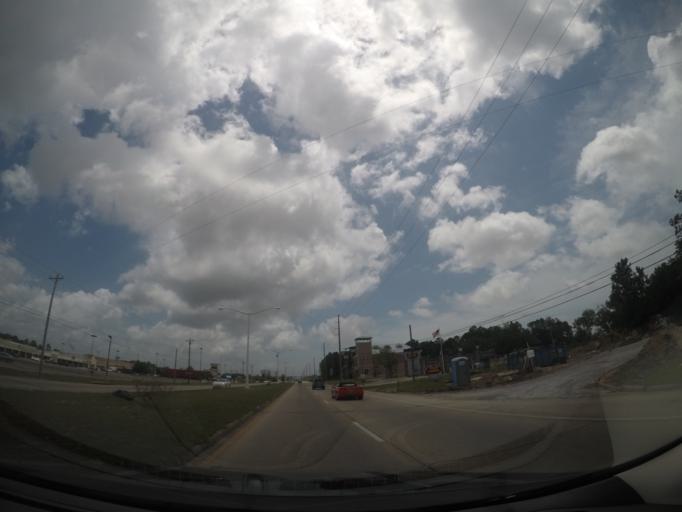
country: US
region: Mississippi
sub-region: Hancock County
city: Waveland
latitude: 30.3044
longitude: -89.3830
